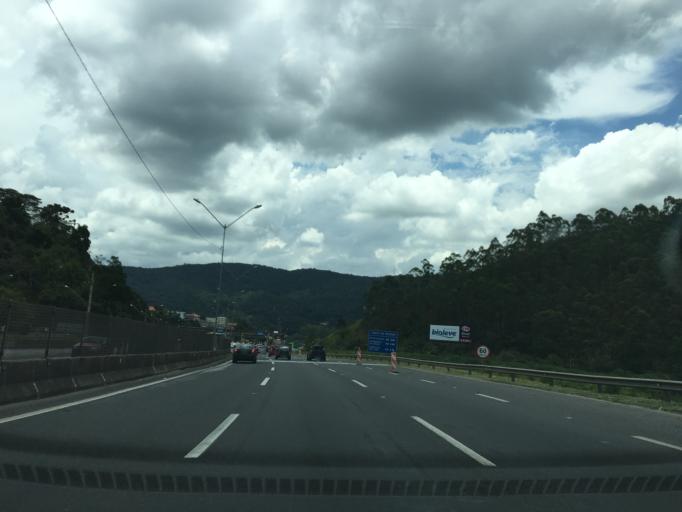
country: BR
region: Sao Paulo
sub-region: Mairipora
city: Mairipora
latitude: -23.3269
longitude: -46.5783
